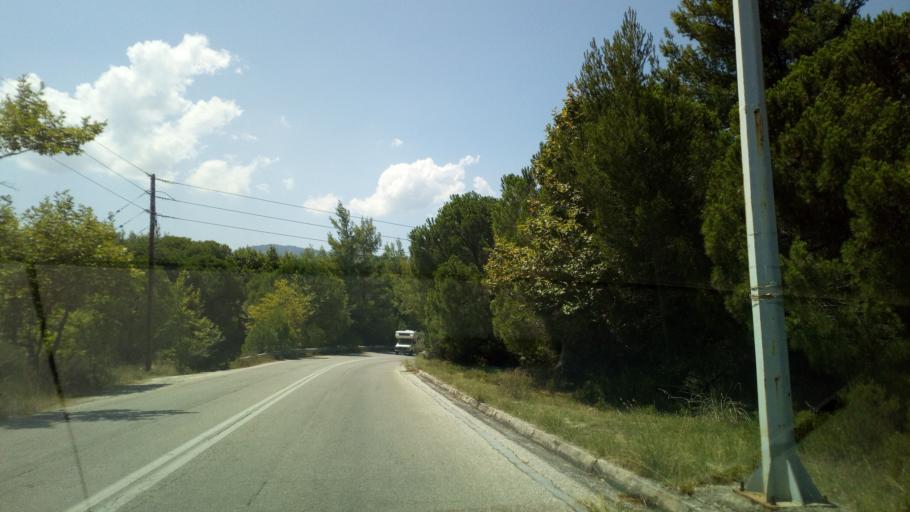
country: GR
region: Central Macedonia
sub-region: Nomos Chalkidikis
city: Sarti
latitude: 40.1167
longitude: 23.9732
